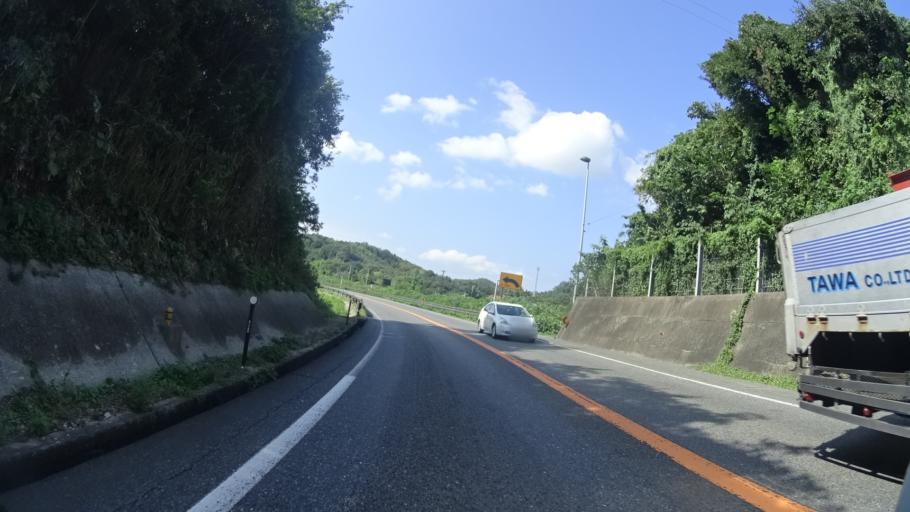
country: JP
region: Shimane
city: Gotsucho
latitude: 35.0565
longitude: 132.3140
